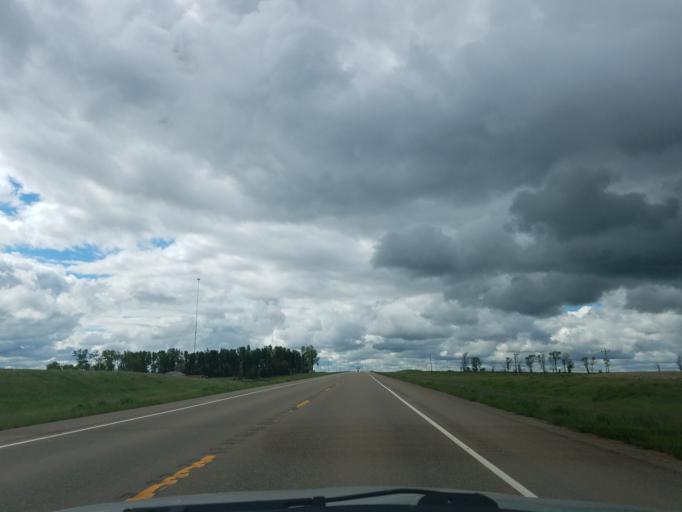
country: US
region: North Dakota
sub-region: McKenzie County
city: Watford City
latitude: 47.4551
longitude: -103.2473
